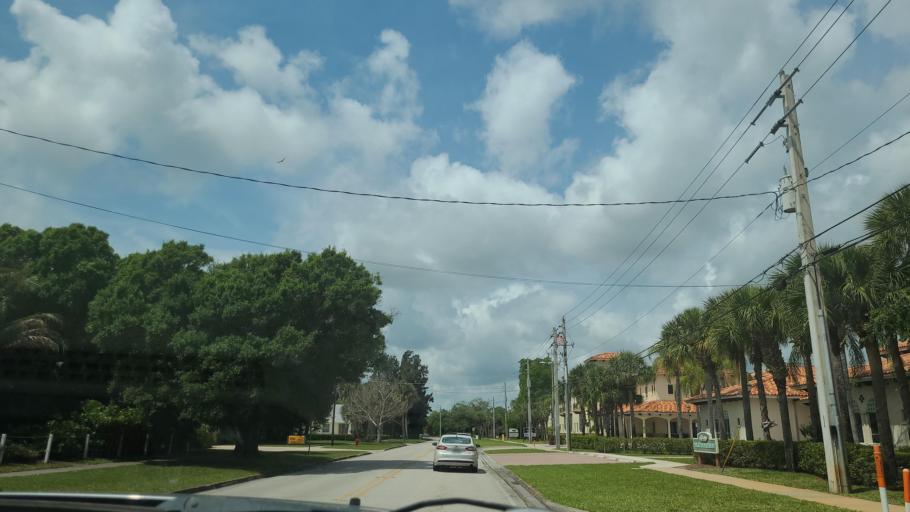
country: US
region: Florida
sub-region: Indian River County
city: Sebastian
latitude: 27.8172
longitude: -80.4738
